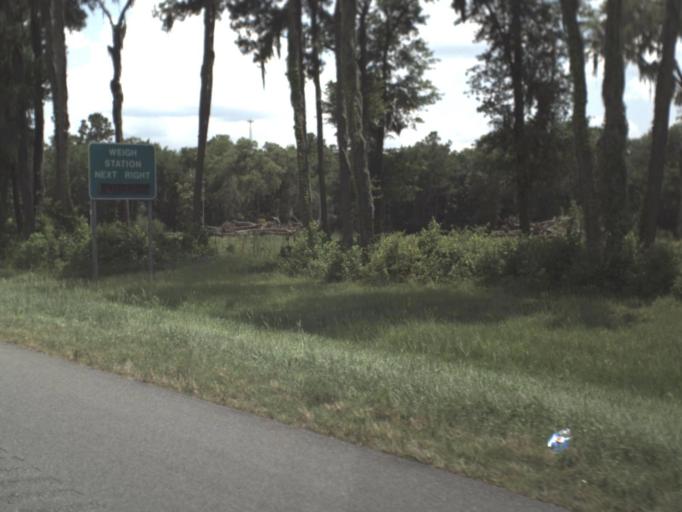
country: US
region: Florida
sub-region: Hamilton County
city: Jasper
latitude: 30.4335
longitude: -82.9121
